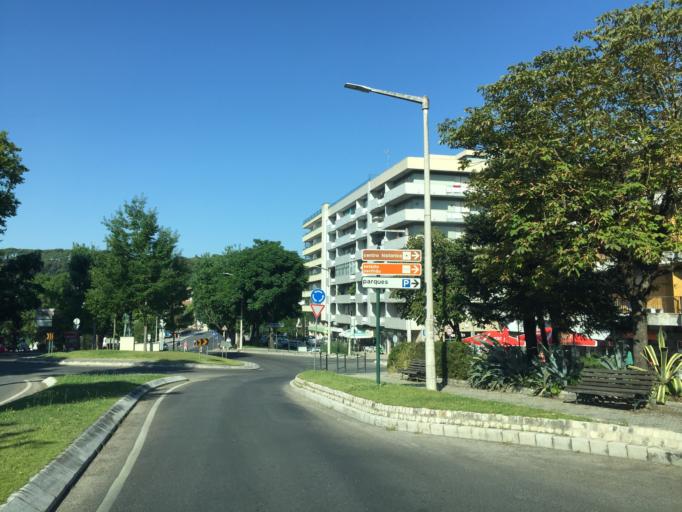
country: PT
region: Santarem
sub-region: Tomar
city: Tomar
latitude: 39.6037
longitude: -8.4089
